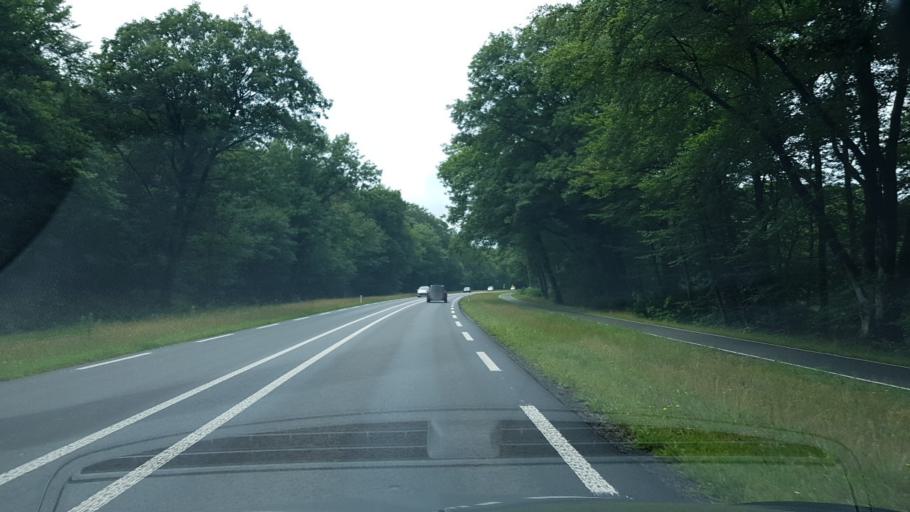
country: NL
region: Gelderland
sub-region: Gemeente Apeldoorn
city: Uddel
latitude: 52.2234
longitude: 5.8326
